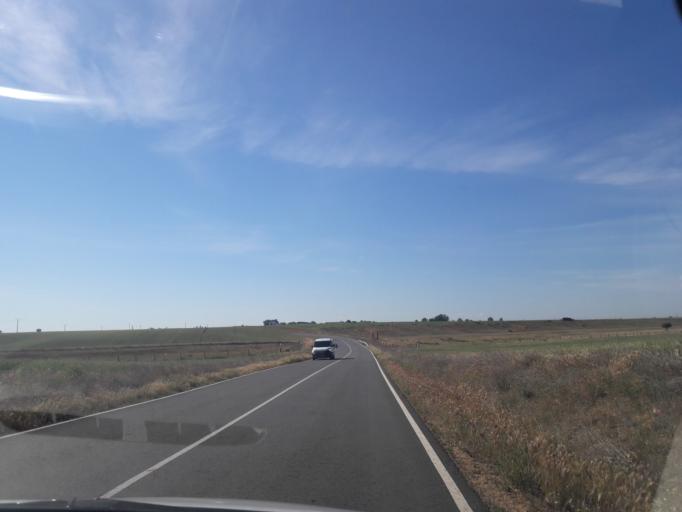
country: ES
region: Castille and Leon
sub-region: Provincia de Salamanca
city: Espino de la Orbada
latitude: 41.0899
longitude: -5.4110
